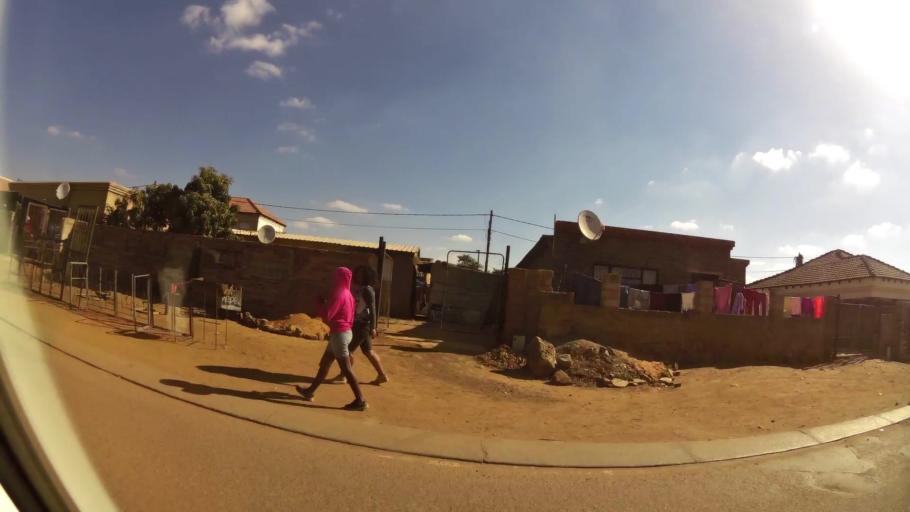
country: ZA
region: Gauteng
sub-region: City of Tshwane Metropolitan Municipality
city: Cullinan
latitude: -25.7188
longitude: 28.4076
